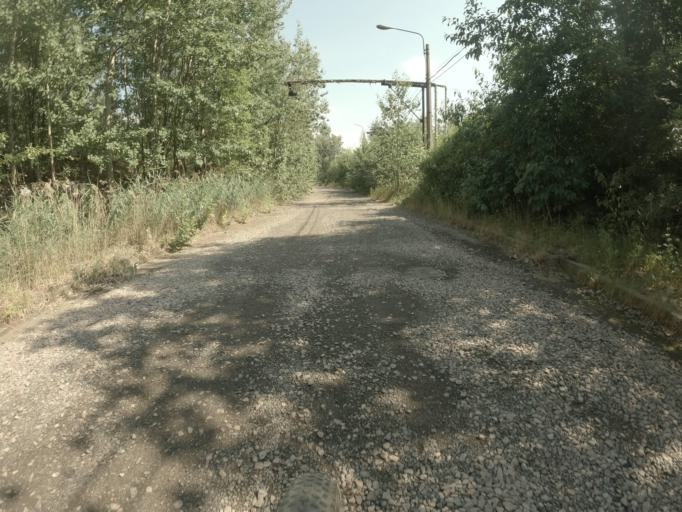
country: RU
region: St.-Petersburg
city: Centralniy
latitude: 59.9153
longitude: 30.4210
